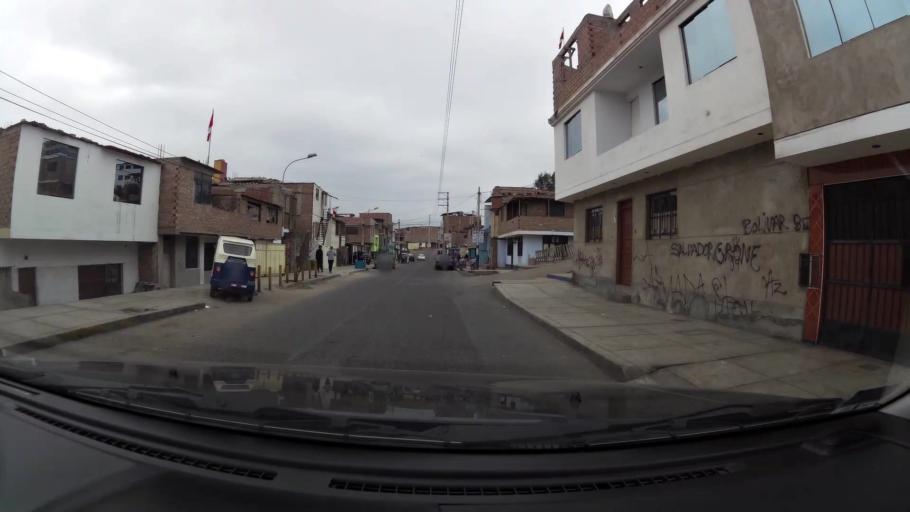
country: PE
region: Lima
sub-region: Lima
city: Surco
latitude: -12.1877
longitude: -76.9898
